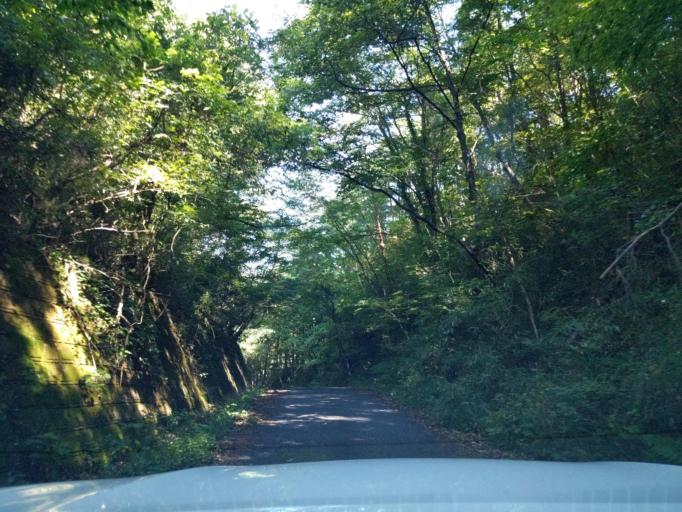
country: JP
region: Fukushima
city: Koriyama
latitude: 37.4006
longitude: 140.2390
